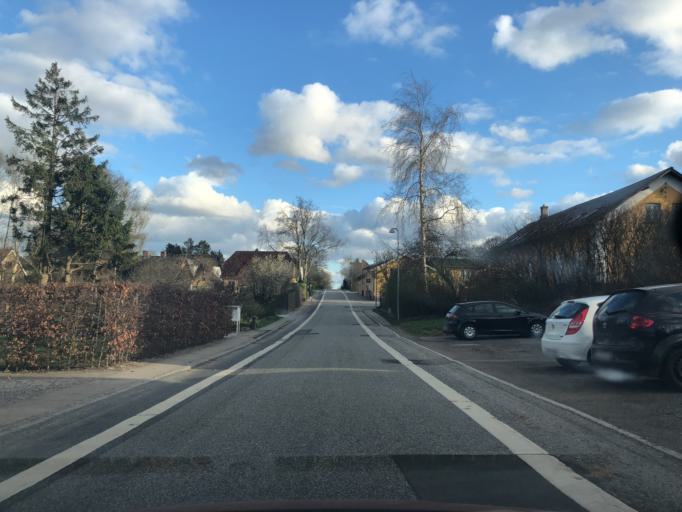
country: DK
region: Zealand
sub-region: Lejre Kommune
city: Kirke Hvalso
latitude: 55.5153
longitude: 11.8660
